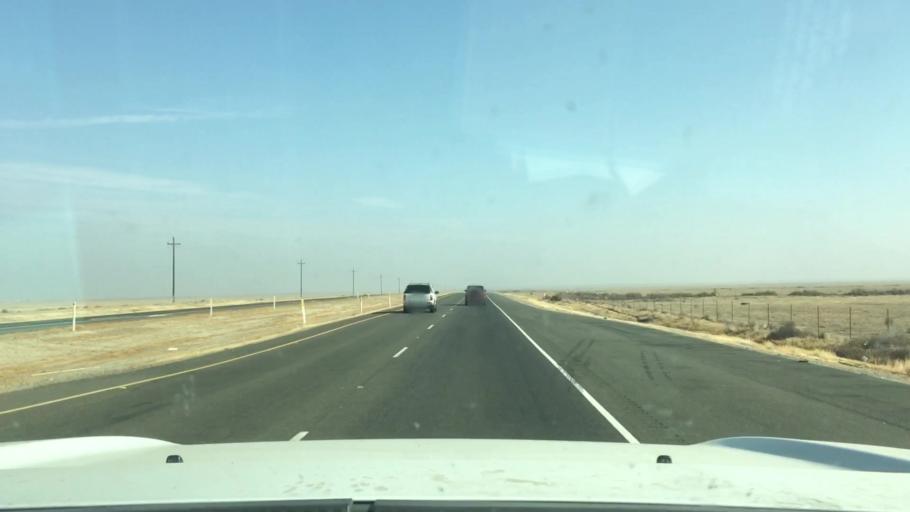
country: US
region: California
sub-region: Kern County
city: Lost Hills
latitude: 35.6153
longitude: -119.8336
